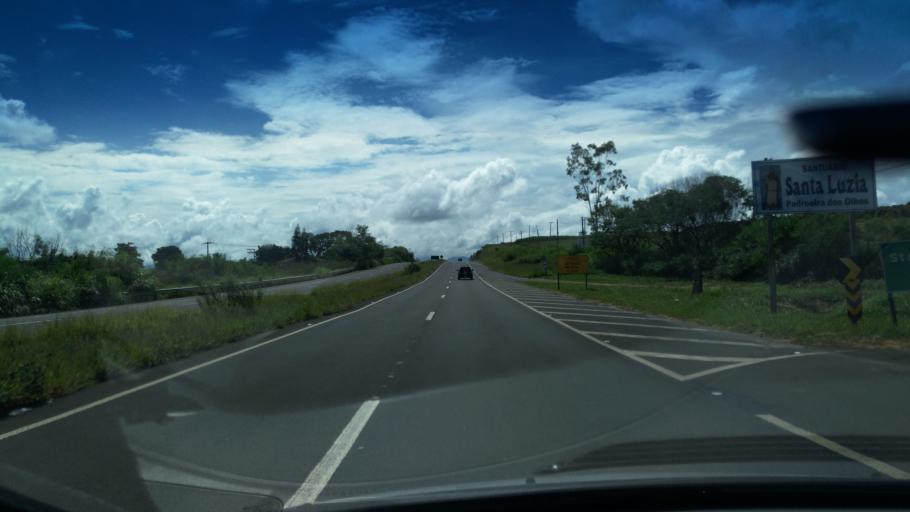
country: BR
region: Sao Paulo
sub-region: Santo Antonio Do Jardim
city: Espirito Santo do Pinhal
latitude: -22.1728
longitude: -46.7455
